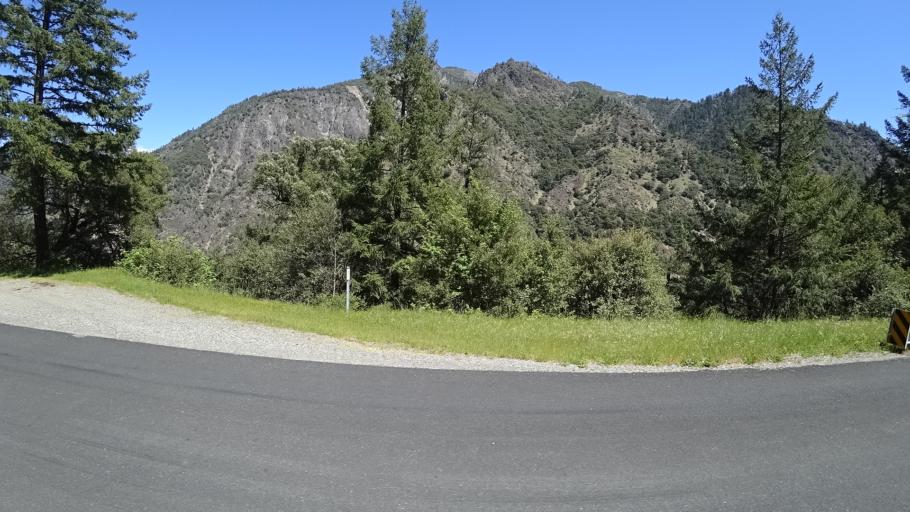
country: US
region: California
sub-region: Humboldt County
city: Willow Creek
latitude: 40.8187
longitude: -123.4803
